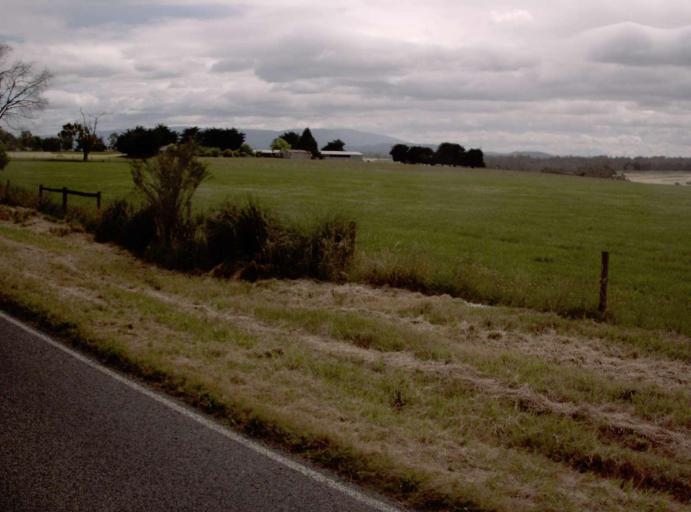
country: AU
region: Victoria
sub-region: Latrobe
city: Moe
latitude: -38.1655
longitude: 146.1431
